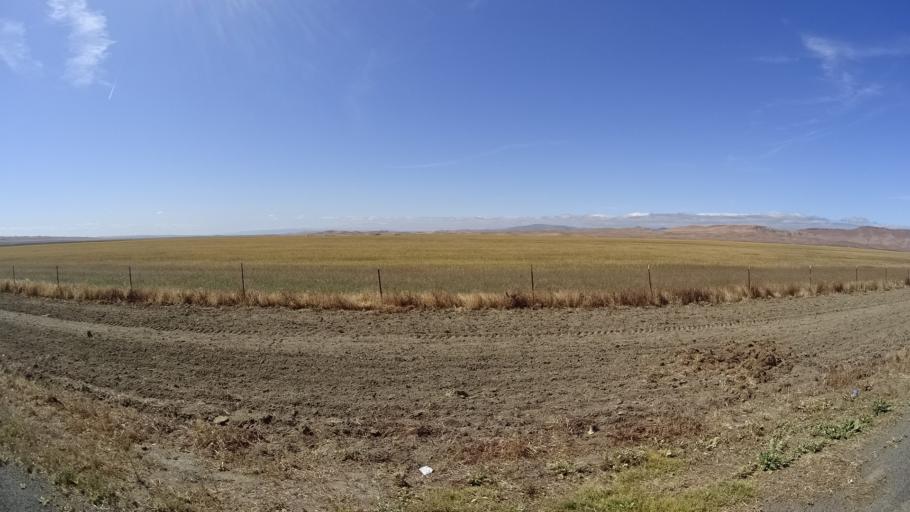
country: US
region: California
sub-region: Kings County
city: Avenal
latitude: 35.9351
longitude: -120.0660
